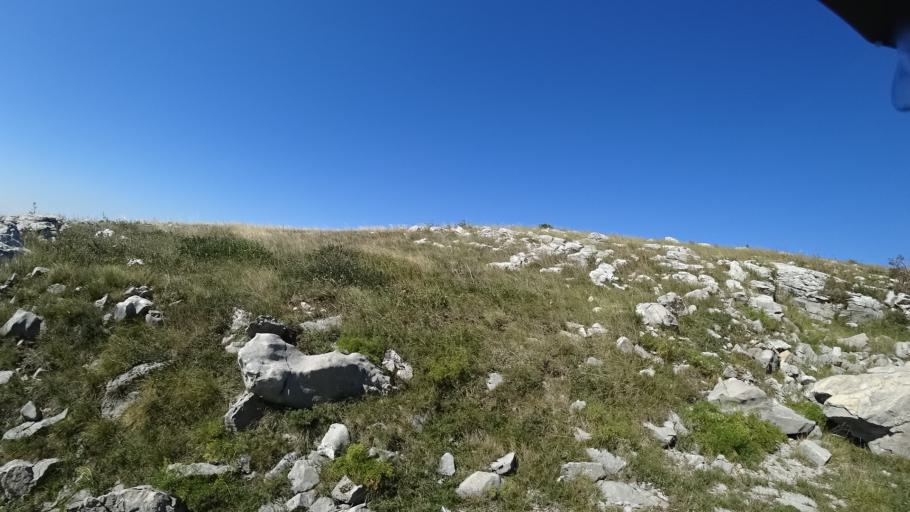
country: HR
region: Splitsko-Dalmatinska
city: Hrvace
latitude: 43.9129
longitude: 16.6099
